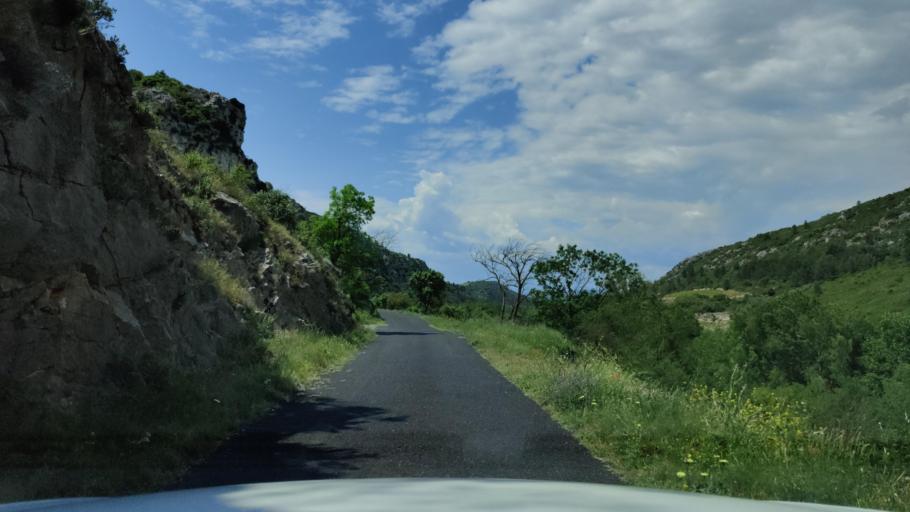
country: FR
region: Languedoc-Roussillon
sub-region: Departement des Pyrenees-Orientales
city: Estagel
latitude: 42.8045
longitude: 2.7361
